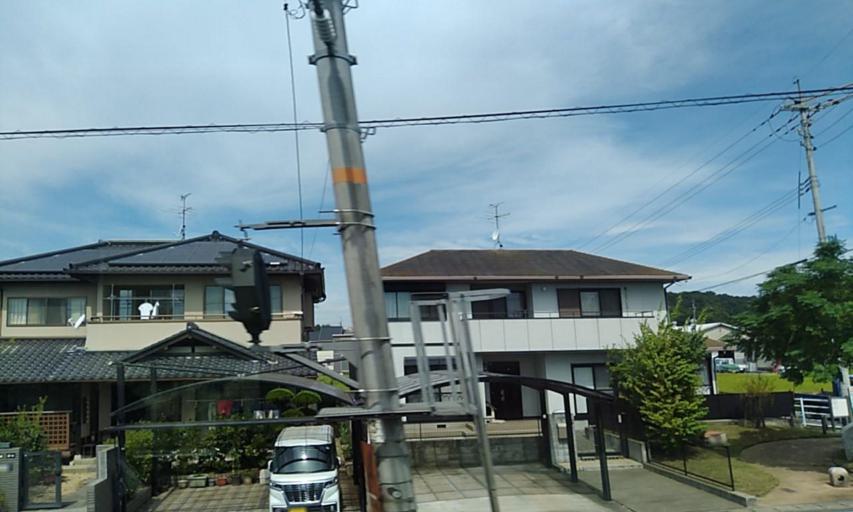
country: JP
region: Okayama
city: Kurashiki
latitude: 34.6042
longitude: 133.8366
